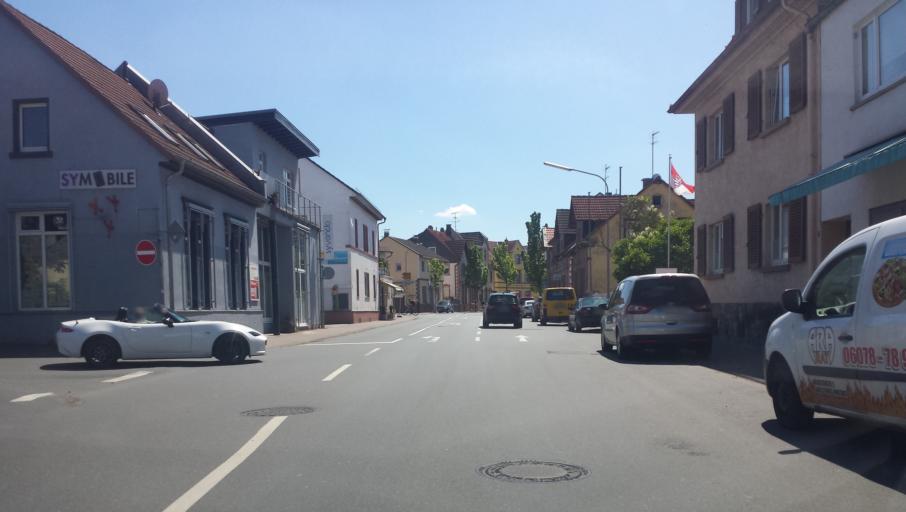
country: DE
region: Hesse
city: Gross-Umstadt
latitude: 49.8660
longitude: 8.9296
